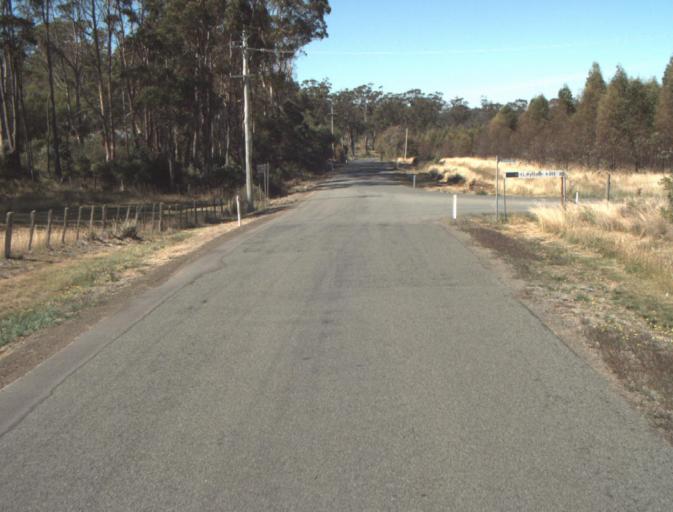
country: AU
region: Tasmania
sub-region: Launceston
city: Newstead
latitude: -41.3792
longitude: 147.2969
